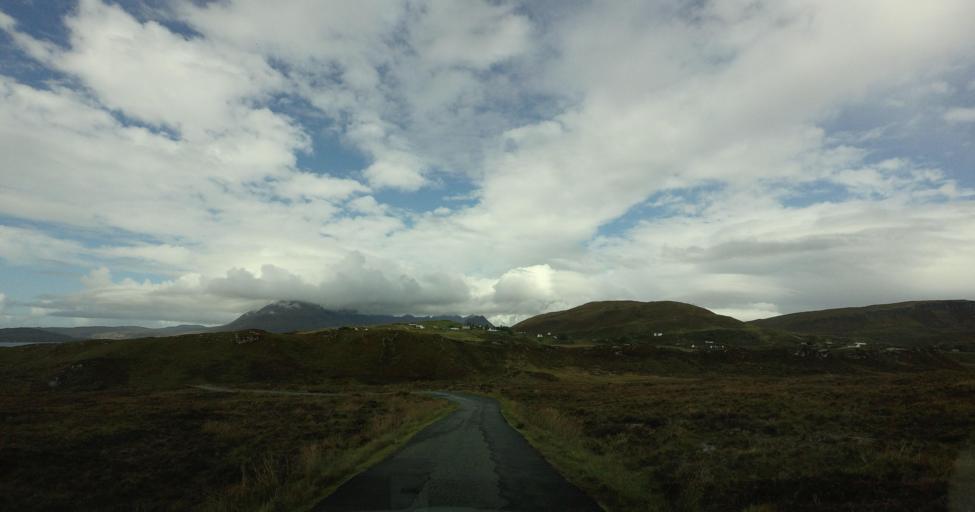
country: GB
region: Scotland
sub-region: Highland
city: Isle of Skye
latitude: 57.1455
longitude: -6.0920
